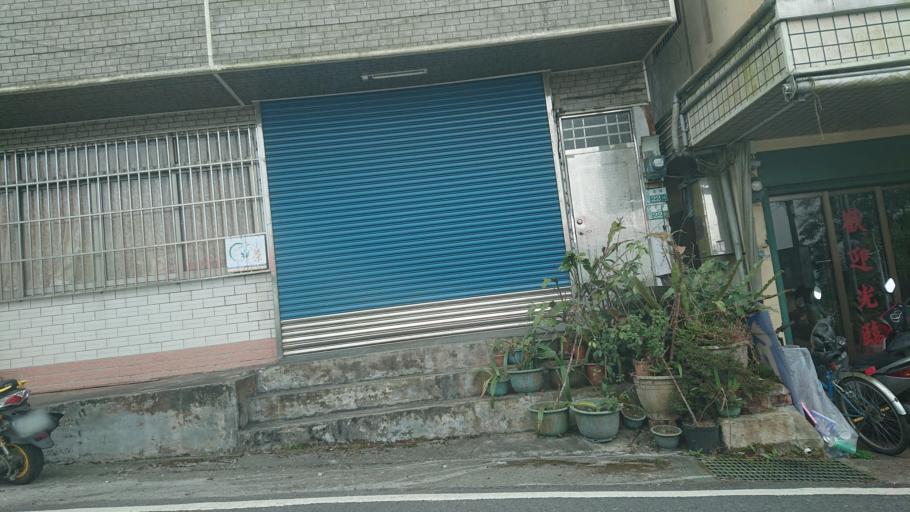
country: TW
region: Taiwan
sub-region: Chiayi
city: Jiayi Shi
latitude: 23.4732
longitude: 120.6984
